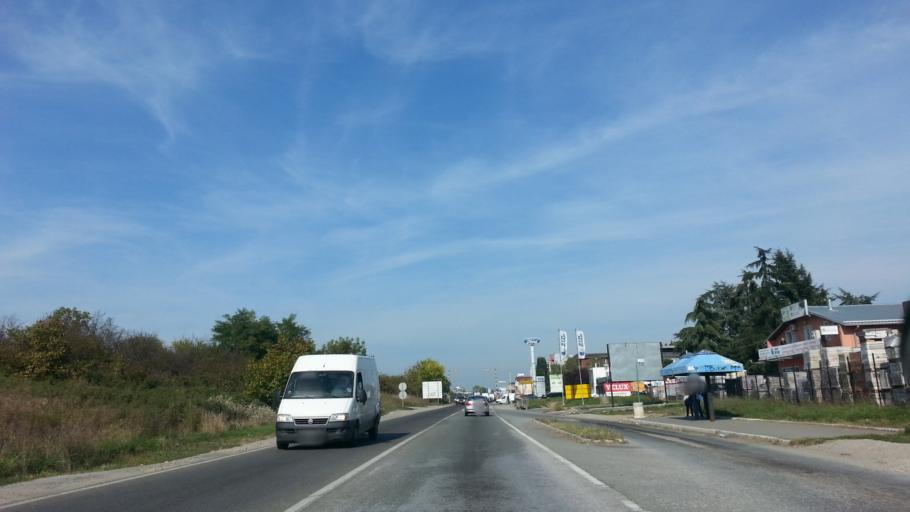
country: RS
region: Central Serbia
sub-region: Belgrade
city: Rakovica
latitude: 44.7215
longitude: 20.4169
